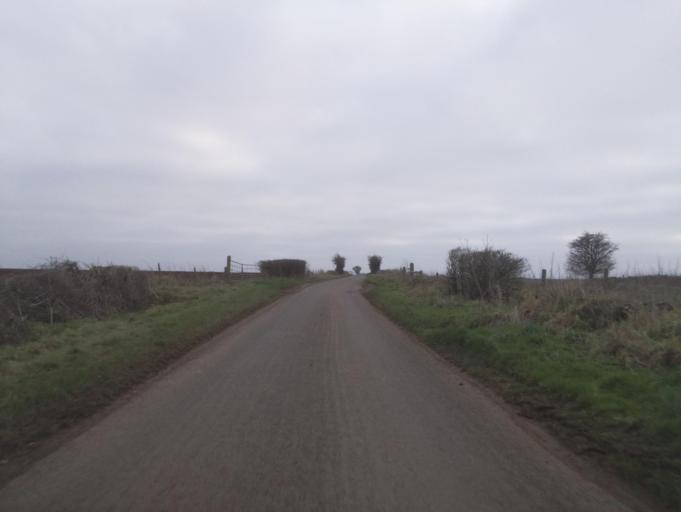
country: GB
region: England
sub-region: Wiltshire
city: Nettleton
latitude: 51.4846
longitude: -2.2826
